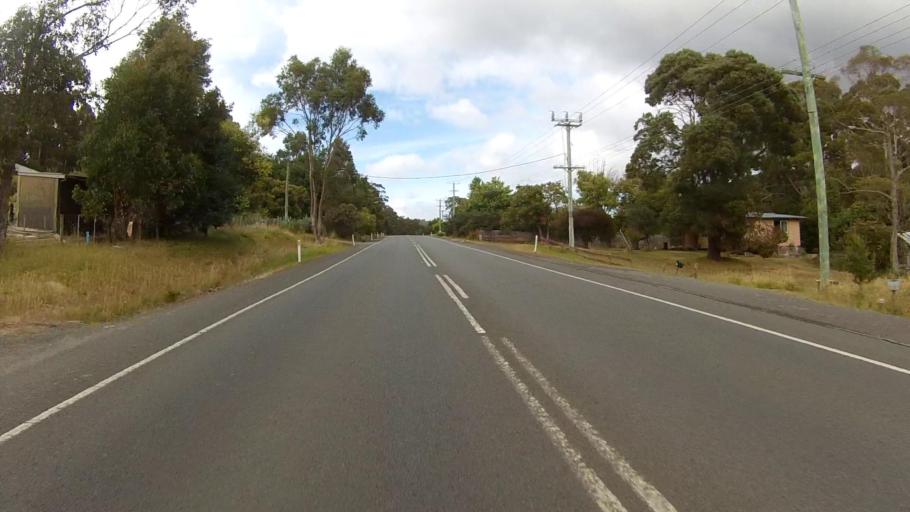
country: AU
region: Tasmania
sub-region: Kingborough
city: Margate
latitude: -43.0768
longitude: 147.2565
